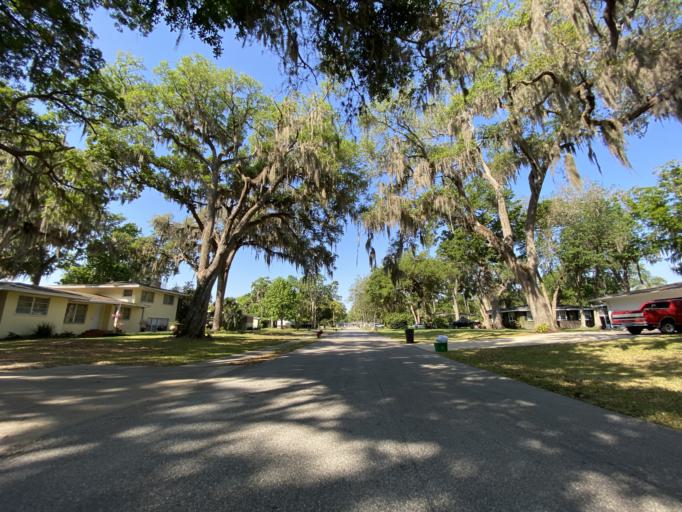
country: US
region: Florida
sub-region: Volusia County
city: South Daytona
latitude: 29.1661
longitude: -81.0144
